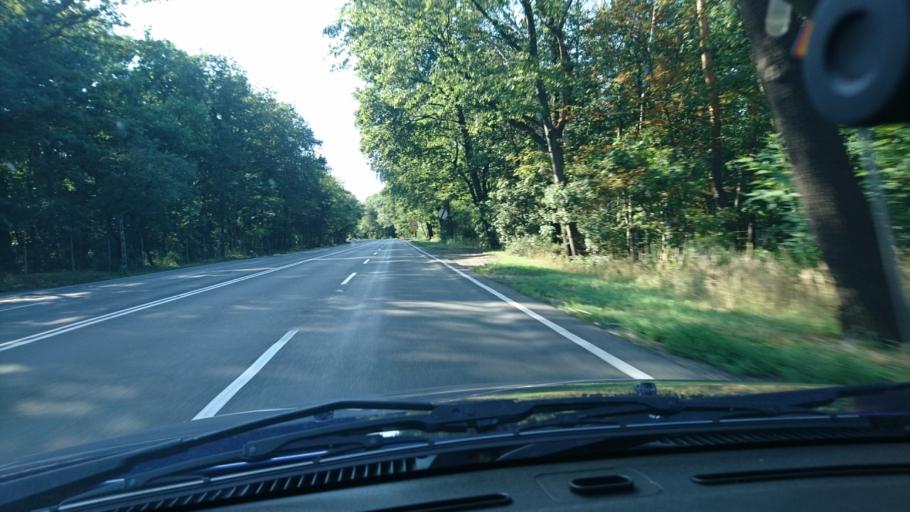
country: PL
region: Silesian Voivodeship
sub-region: Gliwice
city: Gliwice
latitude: 50.3107
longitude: 18.7145
